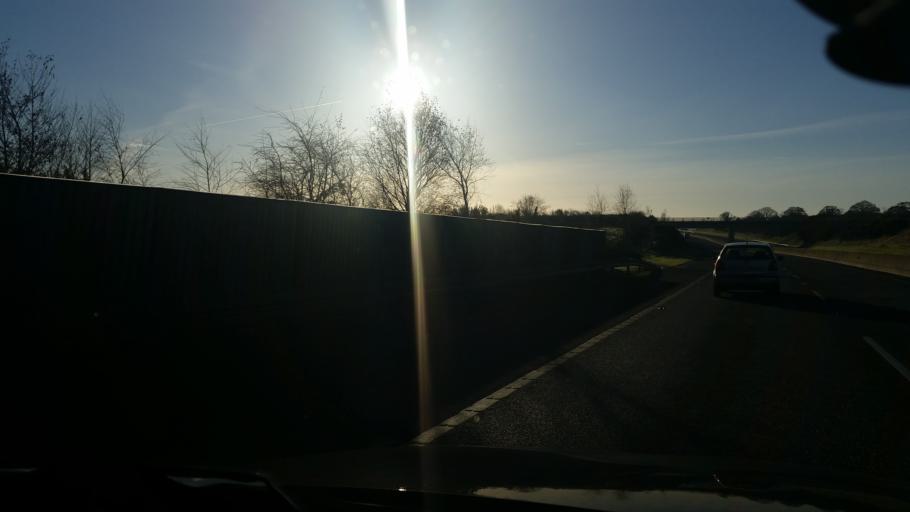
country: IE
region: Leinster
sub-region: Loch Garman
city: Gorey
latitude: 52.6884
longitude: -6.2639
